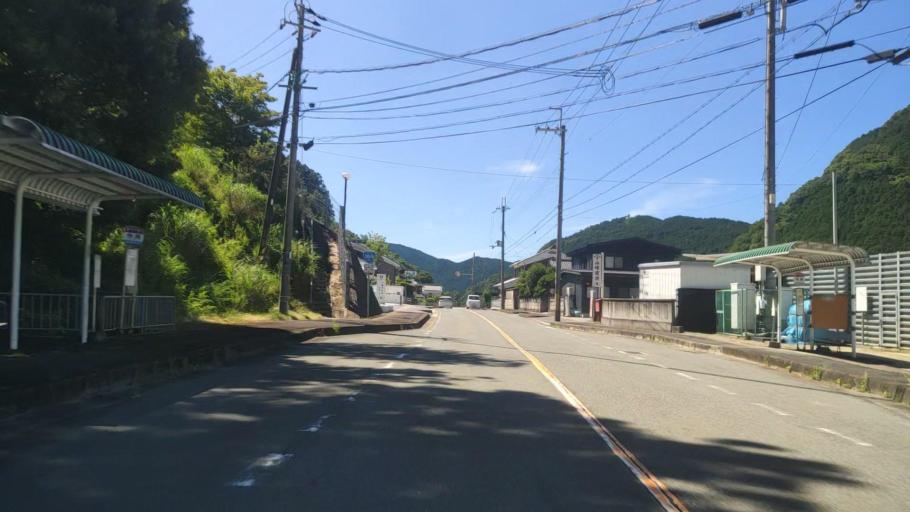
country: JP
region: Nara
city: Yoshino-cho
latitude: 34.3476
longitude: 135.9439
